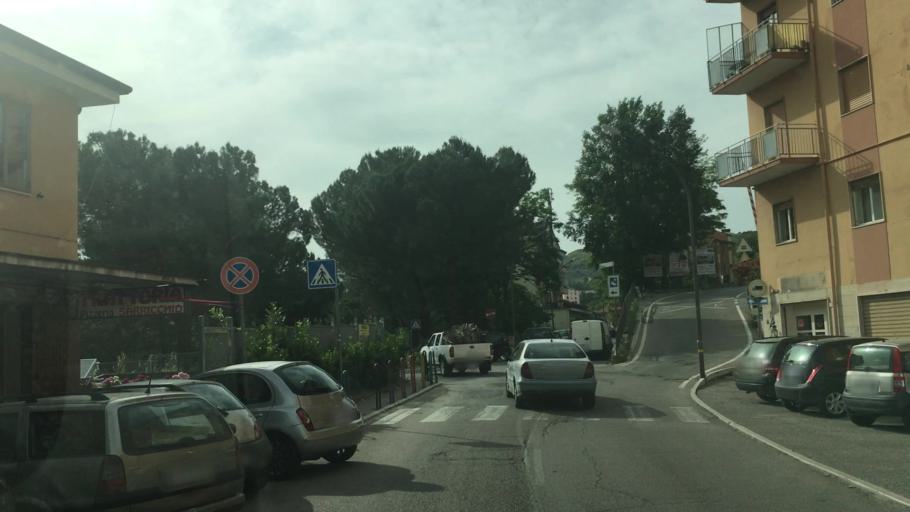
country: IT
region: Basilicate
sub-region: Provincia di Potenza
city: Potenza
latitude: 40.6459
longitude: 15.7995
